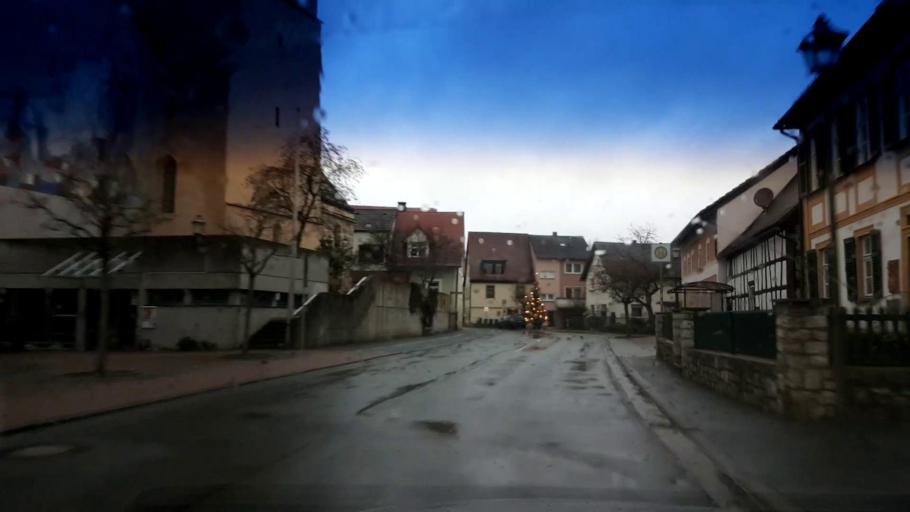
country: DE
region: Bavaria
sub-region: Upper Franconia
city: Litzendorf
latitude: 49.8807
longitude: 11.0139
